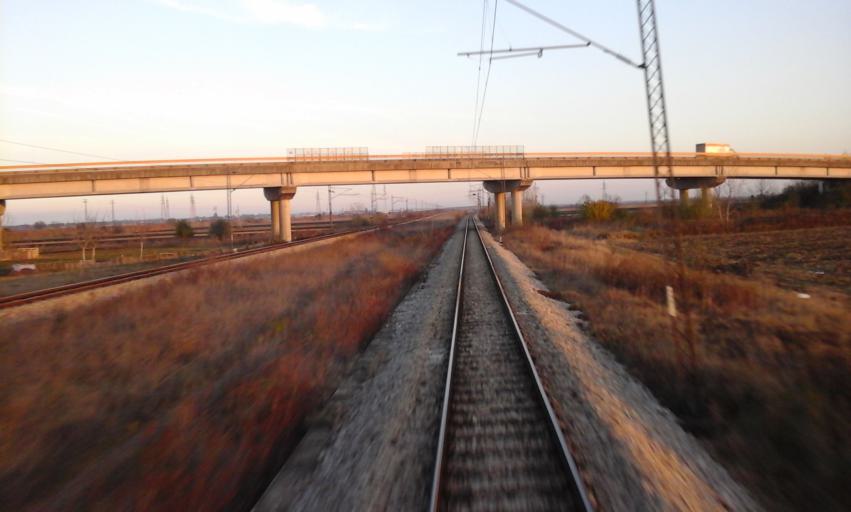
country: RS
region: Autonomna Pokrajina Vojvodina
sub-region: Sremski Okrug
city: Stara Pazova
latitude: 44.9663
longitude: 20.1598
